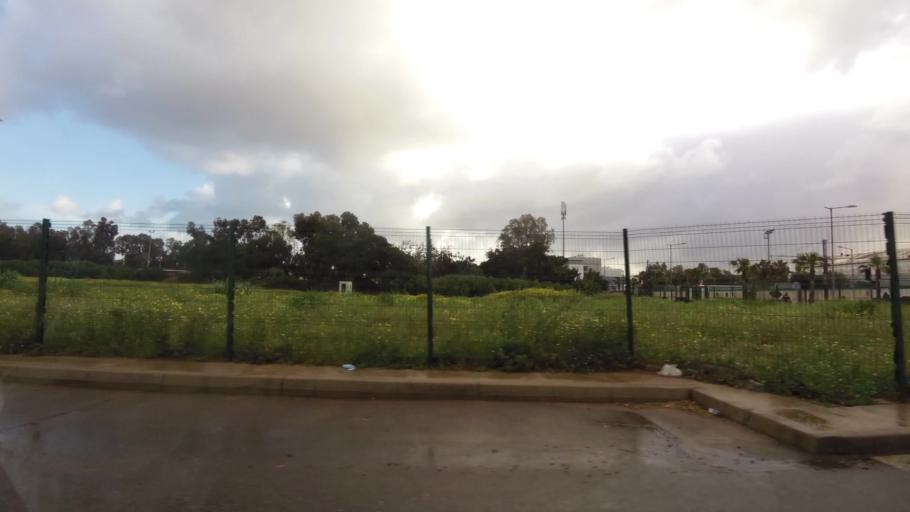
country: MA
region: Grand Casablanca
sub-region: Casablanca
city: Casablanca
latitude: 33.5611
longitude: -7.6506
